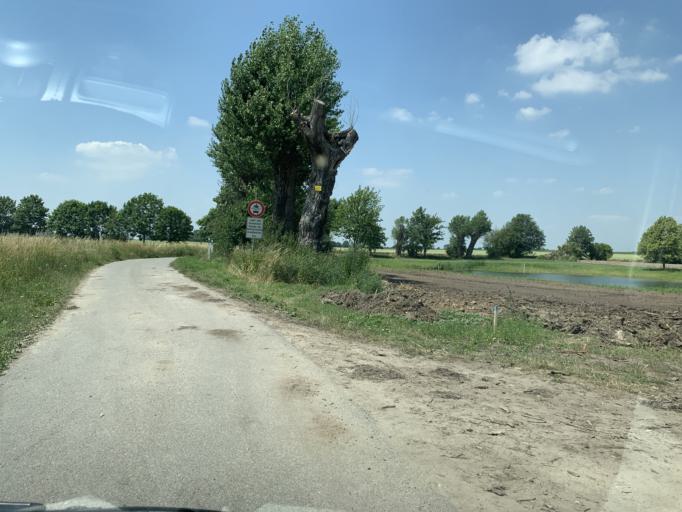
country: DE
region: Saxony-Anhalt
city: Erxleben
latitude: 52.1842
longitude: 11.2611
